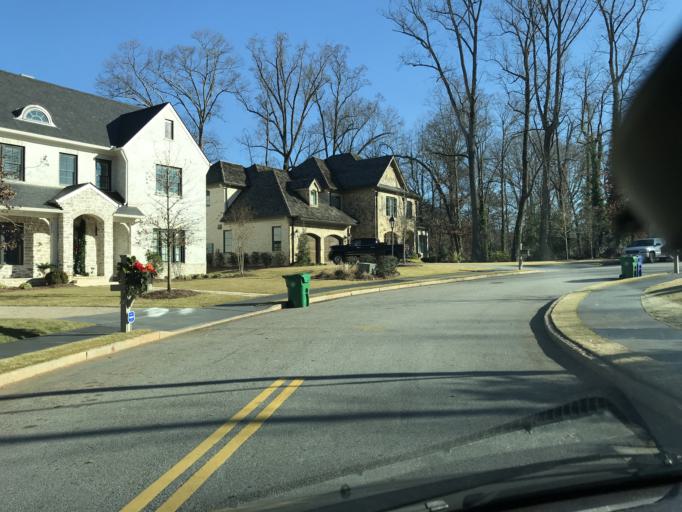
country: US
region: Georgia
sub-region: DeKalb County
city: North Atlanta
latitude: 33.8769
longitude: -84.3475
